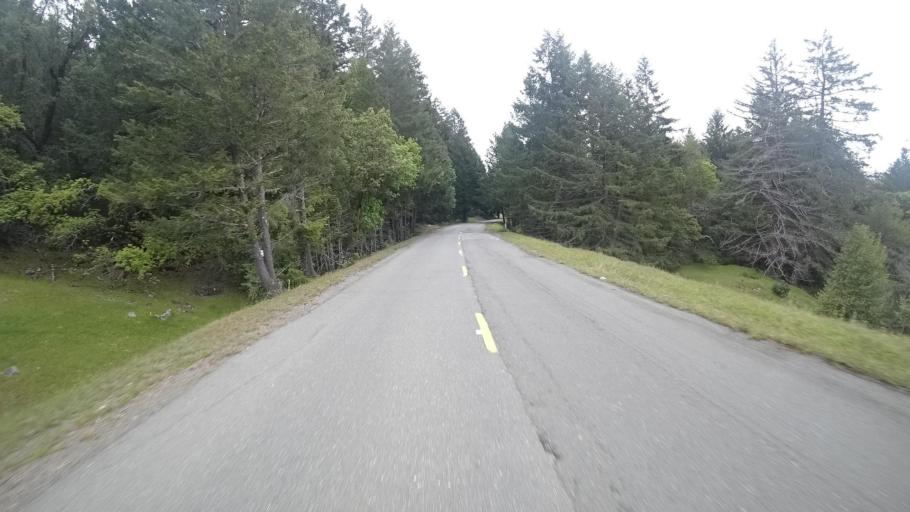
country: US
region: California
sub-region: Humboldt County
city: Redway
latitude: 40.1224
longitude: -123.6624
